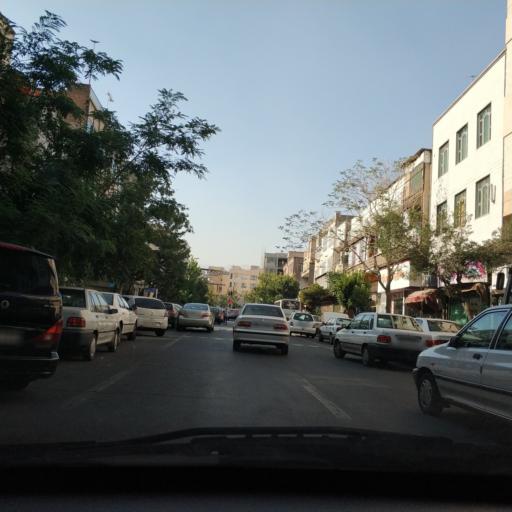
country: IR
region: Tehran
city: Tehran
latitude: 35.7197
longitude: 51.4852
